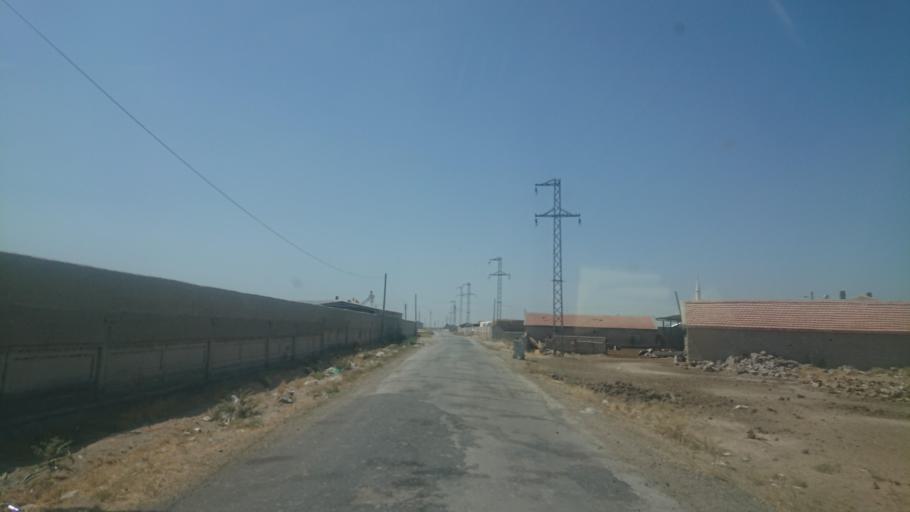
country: TR
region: Aksaray
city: Sultanhani
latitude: 38.2883
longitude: 33.7160
